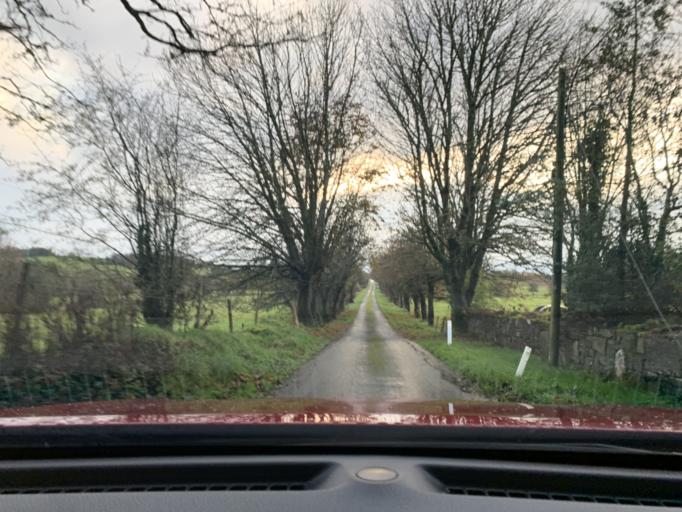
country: IE
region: Connaught
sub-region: Sligo
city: Ballymote
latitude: 54.0340
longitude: -8.5354
